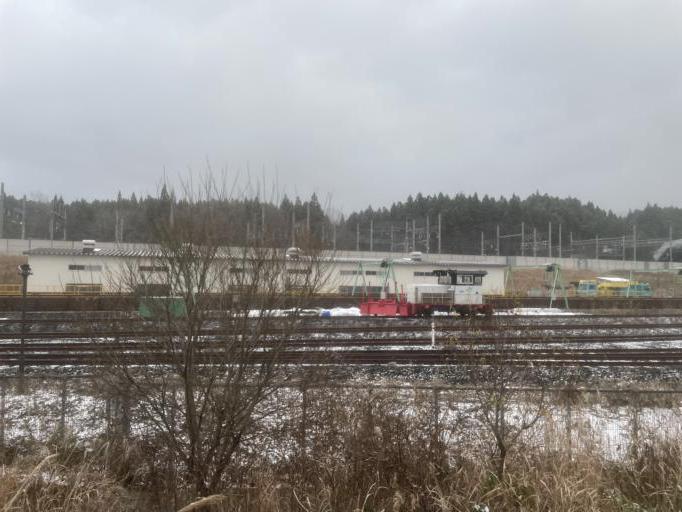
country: JP
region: Aomori
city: Goshogawara
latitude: 41.1418
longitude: 140.5171
